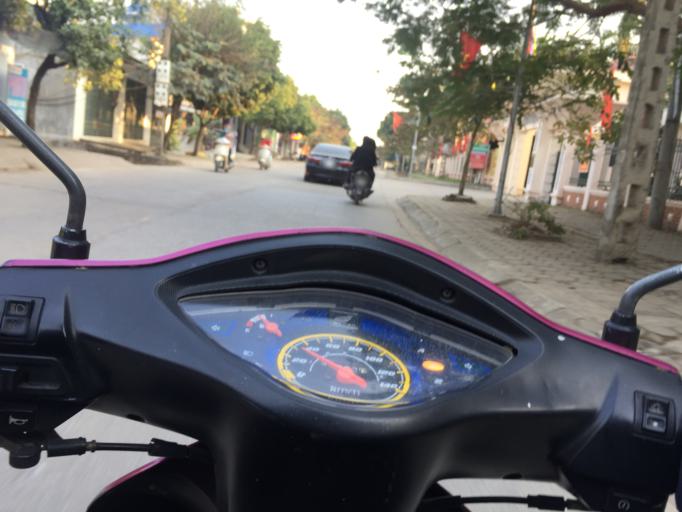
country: VN
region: Ha Noi
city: Chuc Son
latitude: 20.9204
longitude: 105.7123
